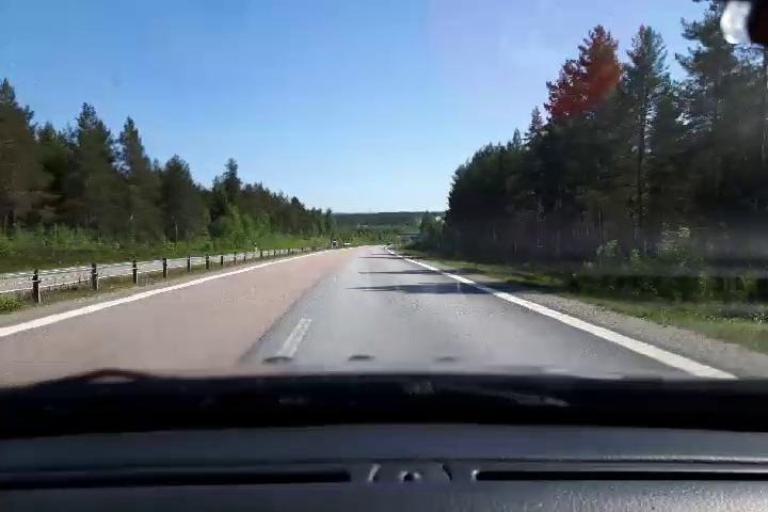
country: SE
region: Gaevleborg
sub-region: Soderhamns Kommun
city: Soderhamn
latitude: 61.3651
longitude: 17.0114
